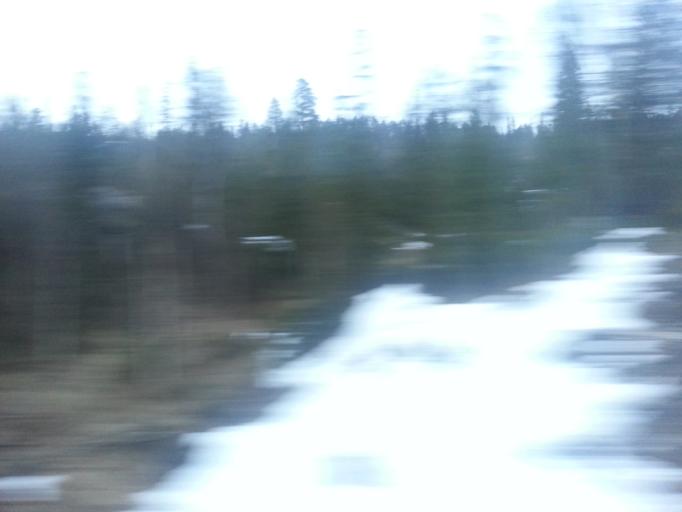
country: NO
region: Sor-Trondelag
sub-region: Rennebu
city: Berkak
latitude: 62.7883
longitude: 10.0051
